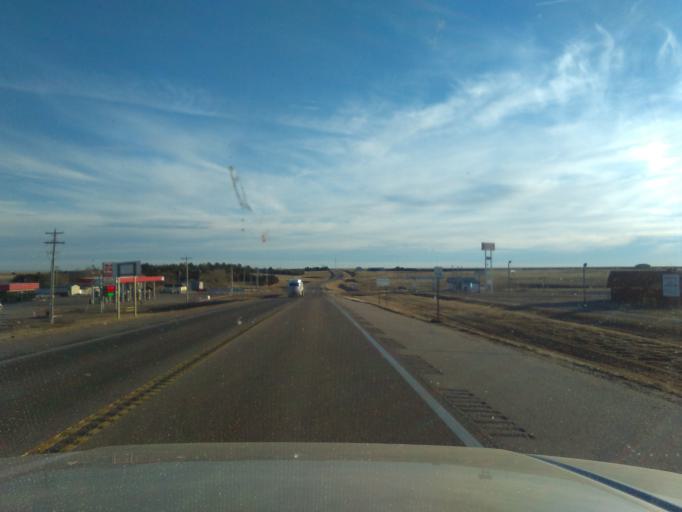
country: US
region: Kansas
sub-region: Logan County
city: Oakley
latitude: 39.1874
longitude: -100.8699
